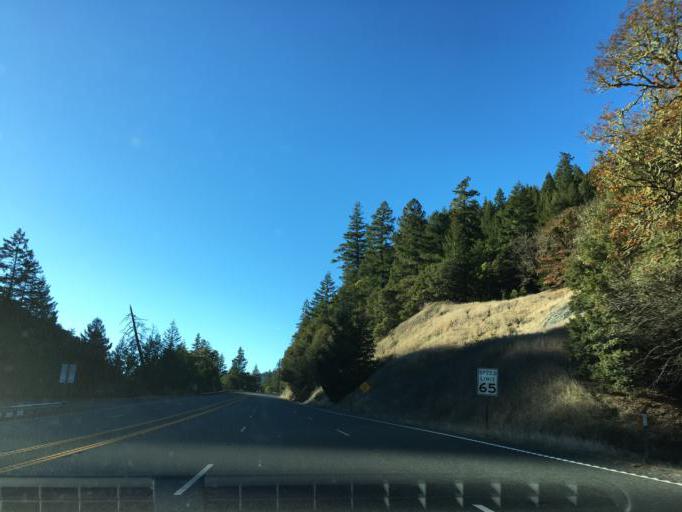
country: US
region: California
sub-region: Mendocino County
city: Laytonville
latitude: 39.8328
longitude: -123.6216
